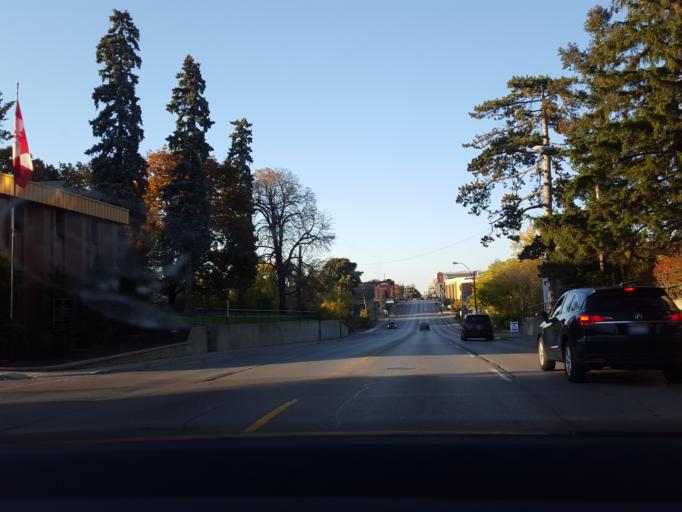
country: CA
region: Ontario
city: Newmarket
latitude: 43.9948
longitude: -79.4664
